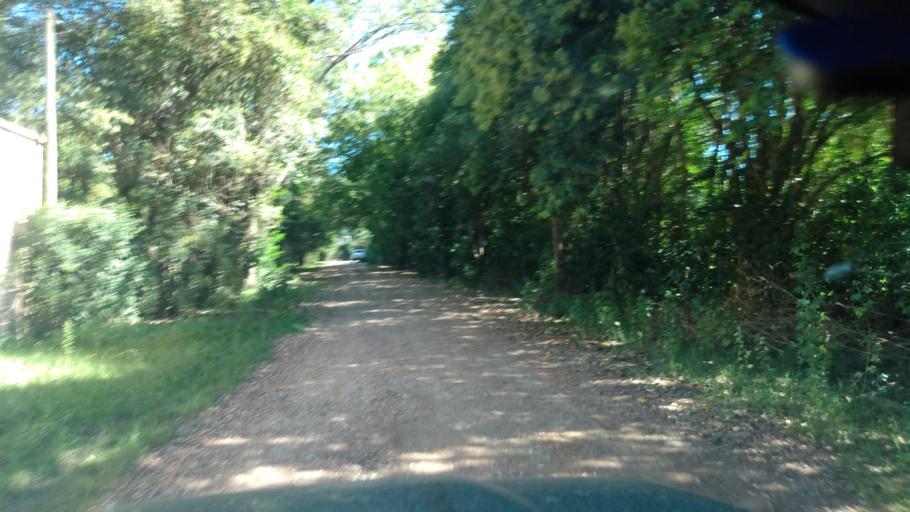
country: AR
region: Buenos Aires
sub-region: Partido de Lujan
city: Lujan
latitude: -34.5511
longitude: -59.1484
